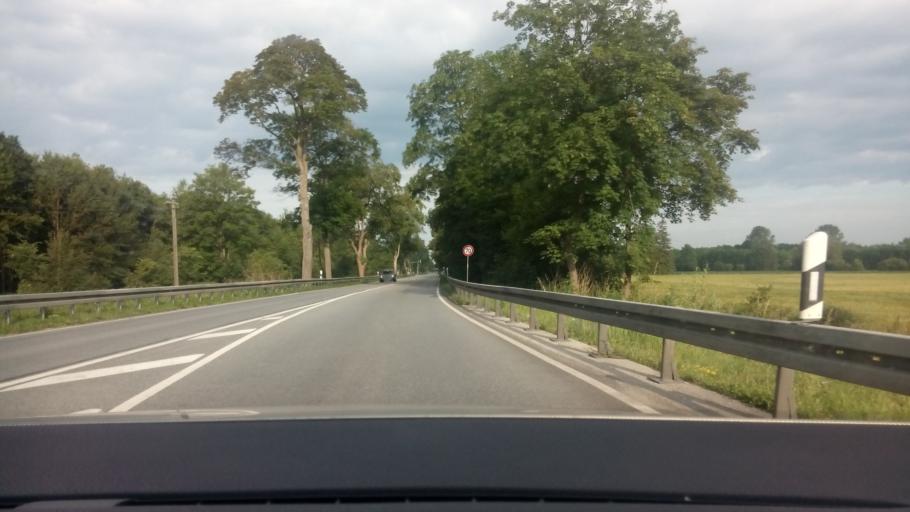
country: DE
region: Bavaria
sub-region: Upper Bavaria
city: Oberschleissheim
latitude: 48.2534
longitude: 11.5133
